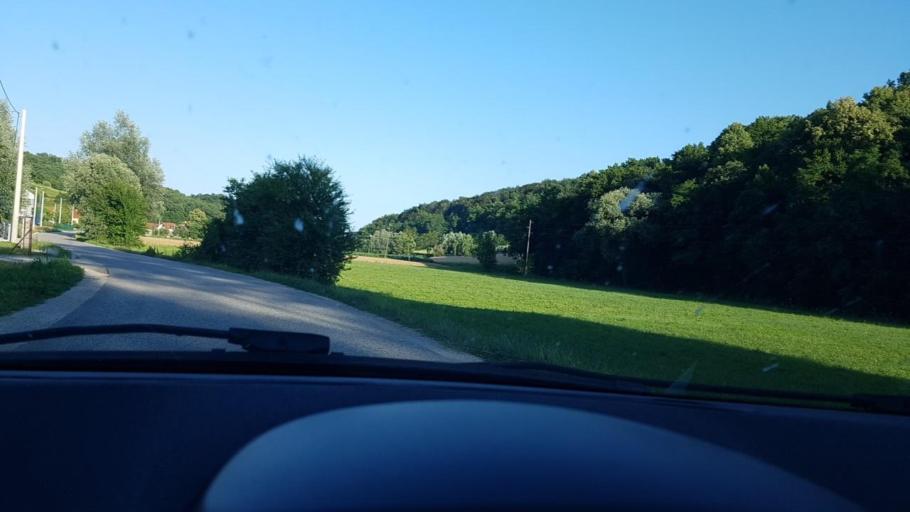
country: HR
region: Krapinsko-Zagorska
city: Bedekovcina
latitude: 46.0802
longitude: 15.9798
